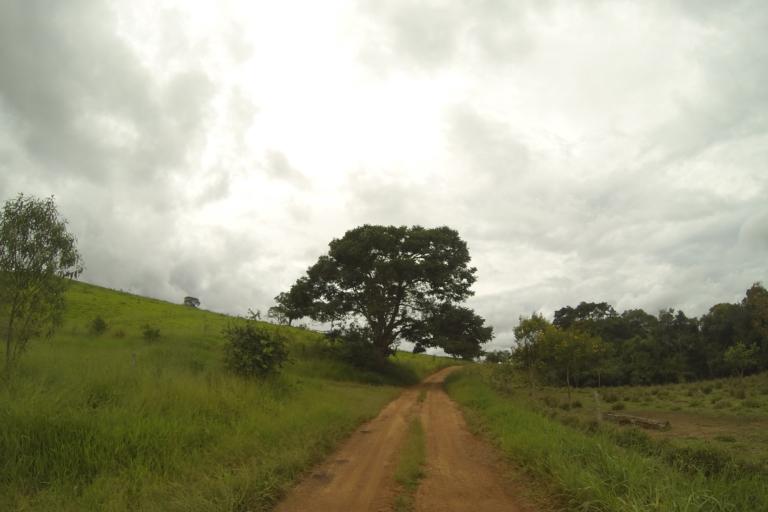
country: BR
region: Minas Gerais
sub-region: Ibia
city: Ibia
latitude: -19.7224
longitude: -46.5706
